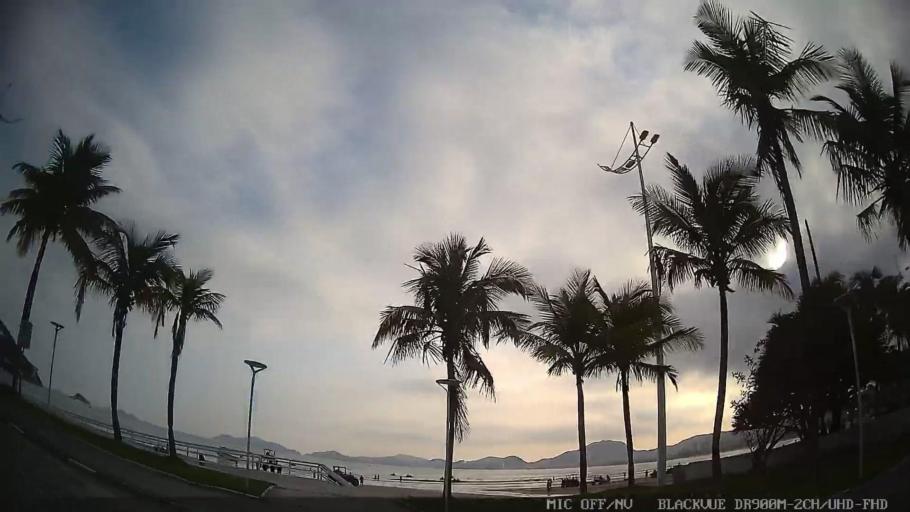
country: BR
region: Sao Paulo
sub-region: Guaruja
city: Guaruja
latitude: -23.9909
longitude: -46.2024
